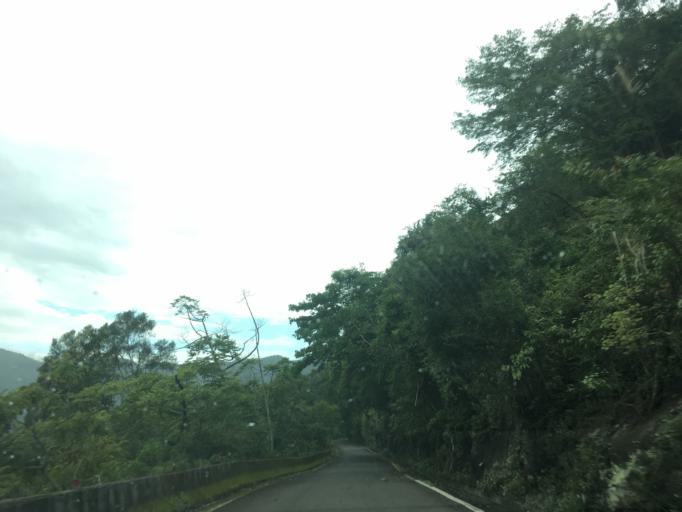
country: TW
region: Taiwan
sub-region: Yunlin
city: Douliu
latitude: 23.5716
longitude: 120.6401
